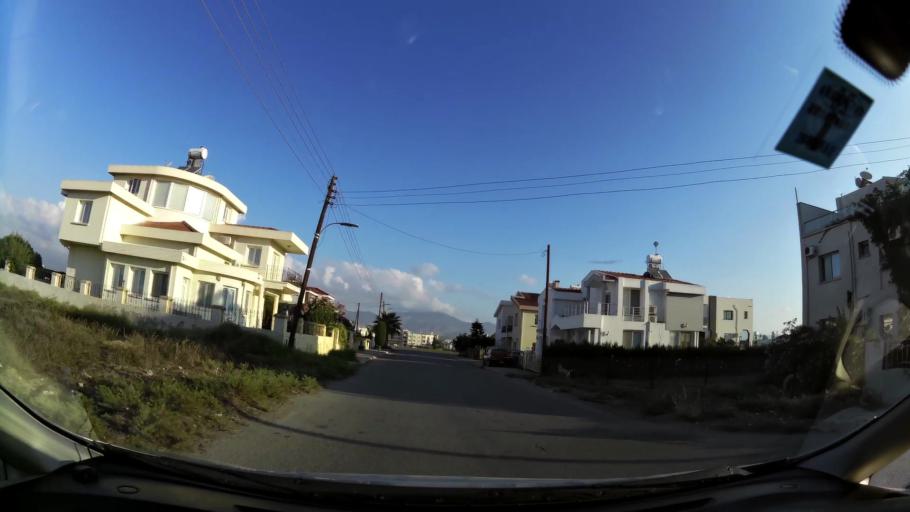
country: CY
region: Lefkosia
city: Nicosia
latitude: 35.1963
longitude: 33.3254
